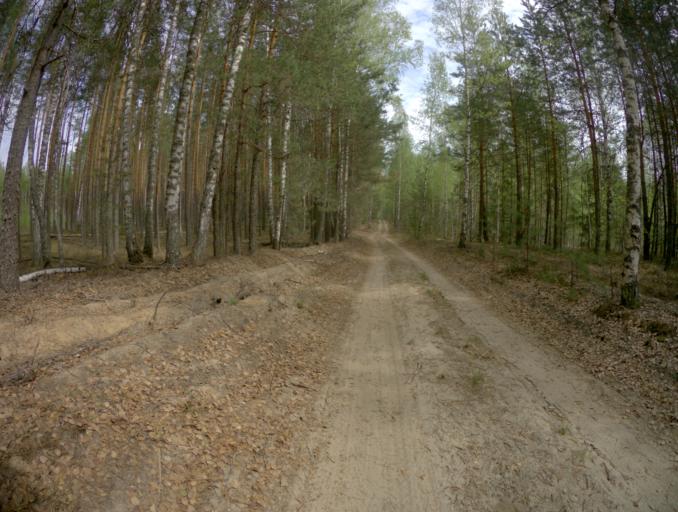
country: RU
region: Ivanovo
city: Yuzha
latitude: 56.4872
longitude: 42.1546
